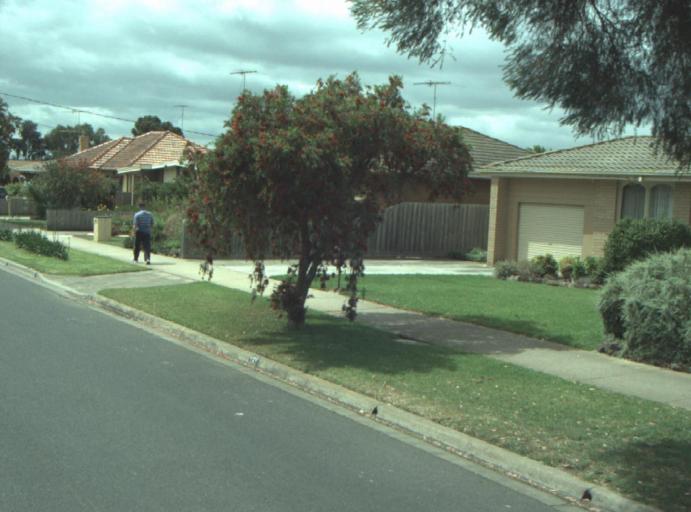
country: AU
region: Victoria
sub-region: Greater Geelong
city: Bell Park
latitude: -38.0663
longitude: 144.3566
